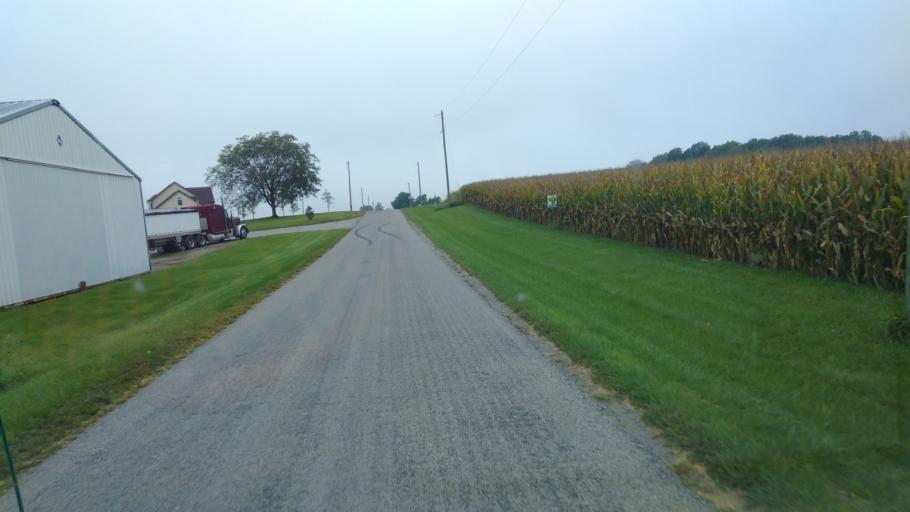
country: US
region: Ohio
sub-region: Union County
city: Richwood
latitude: 40.5014
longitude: -83.3441
